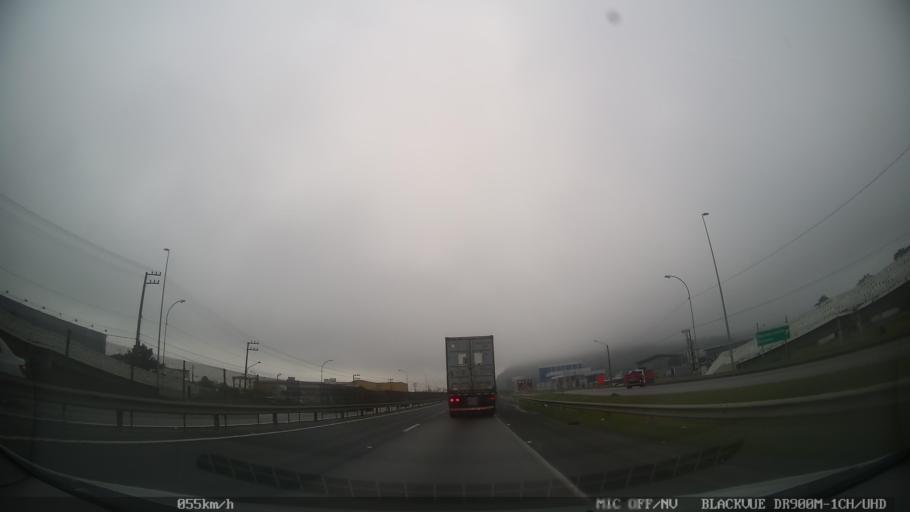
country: BR
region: Santa Catarina
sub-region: Itajai
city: Itajai
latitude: -26.8488
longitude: -48.7244
